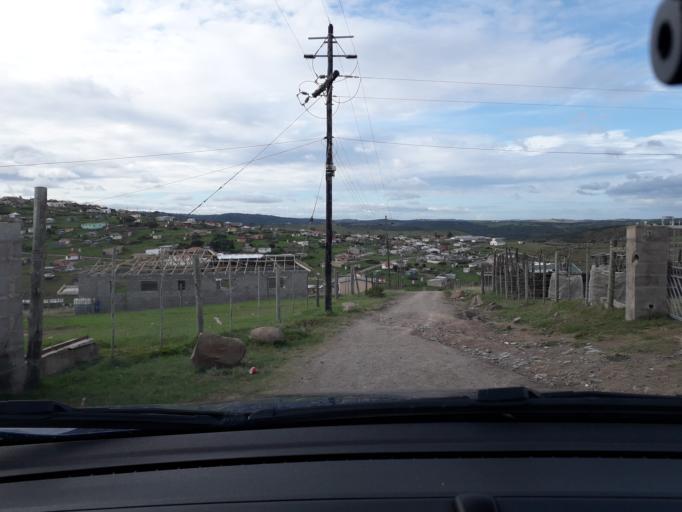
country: ZA
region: Eastern Cape
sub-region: Buffalo City Metropolitan Municipality
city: East London
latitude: -32.8506
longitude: 27.9848
